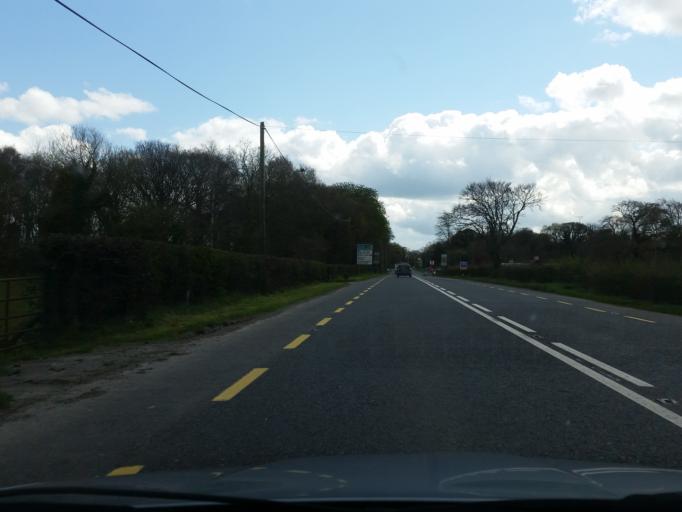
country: IE
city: Kentstown
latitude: 53.6429
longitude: -6.5029
